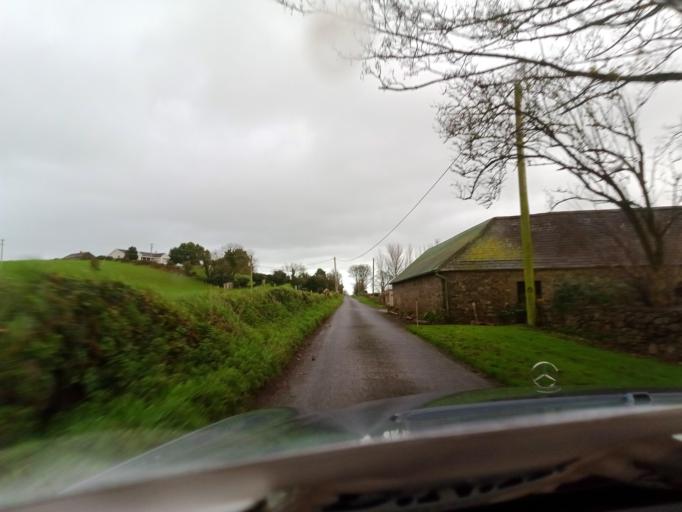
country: IE
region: Leinster
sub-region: Kilkenny
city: Mooncoin
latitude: 52.2641
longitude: -7.1952
